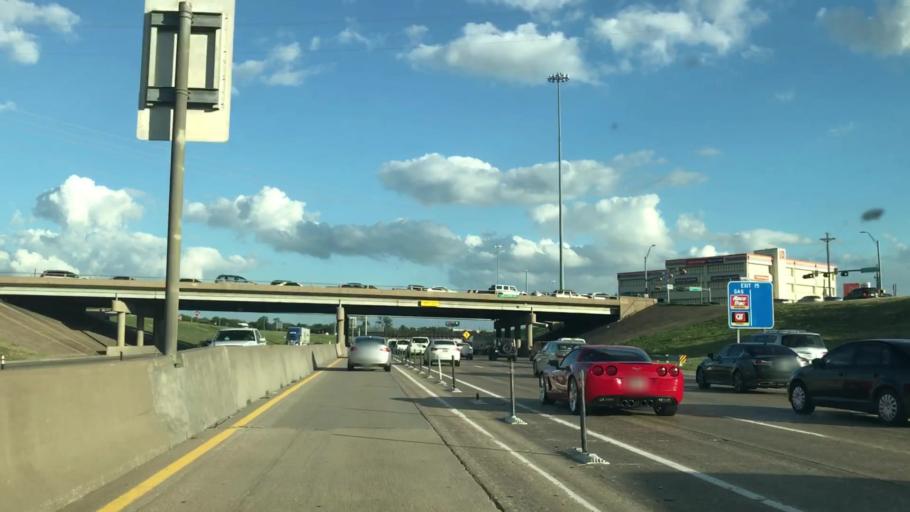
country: US
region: Texas
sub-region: Dallas County
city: Richardson
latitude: 32.9010
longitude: -96.7186
